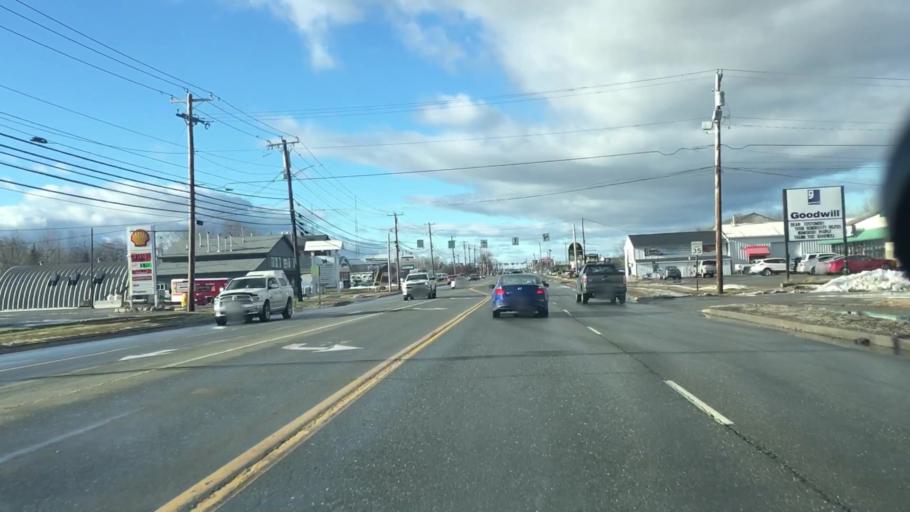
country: US
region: Maine
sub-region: Penobscot County
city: Brewer
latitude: 44.7782
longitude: -68.7373
